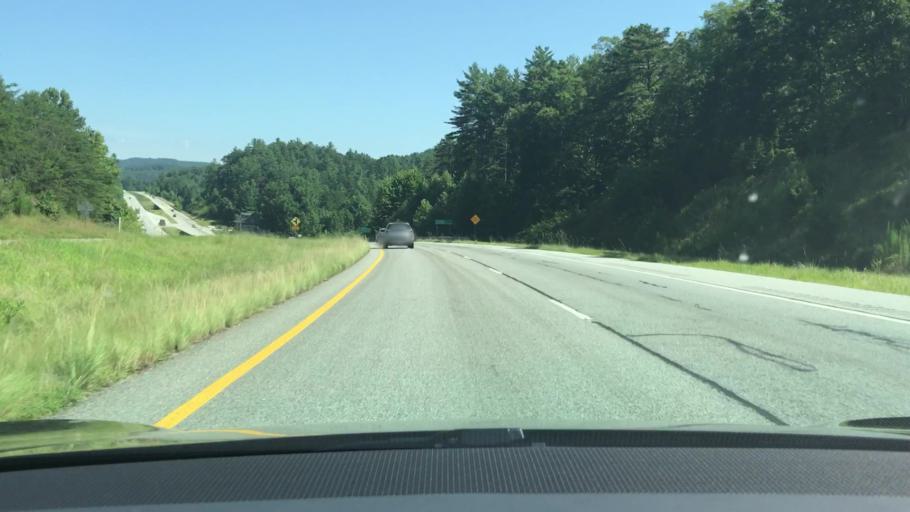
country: US
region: Georgia
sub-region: Rabun County
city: Clayton
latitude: 34.7542
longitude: -83.3965
